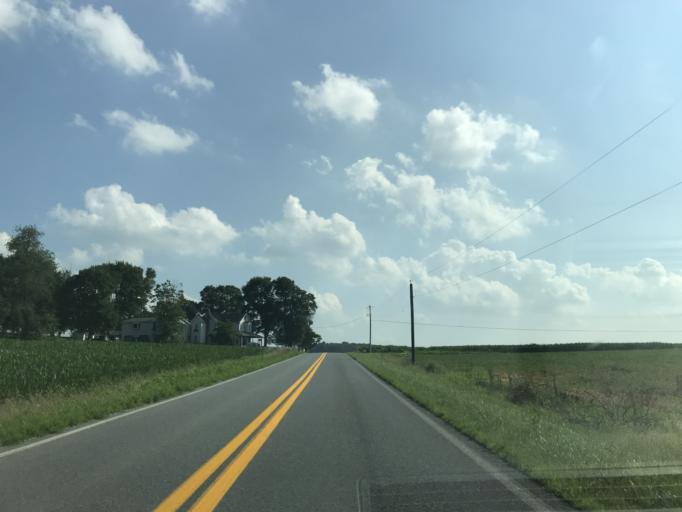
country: US
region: Maryland
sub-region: Carroll County
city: Manchester
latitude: 39.6455
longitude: -76.9379
